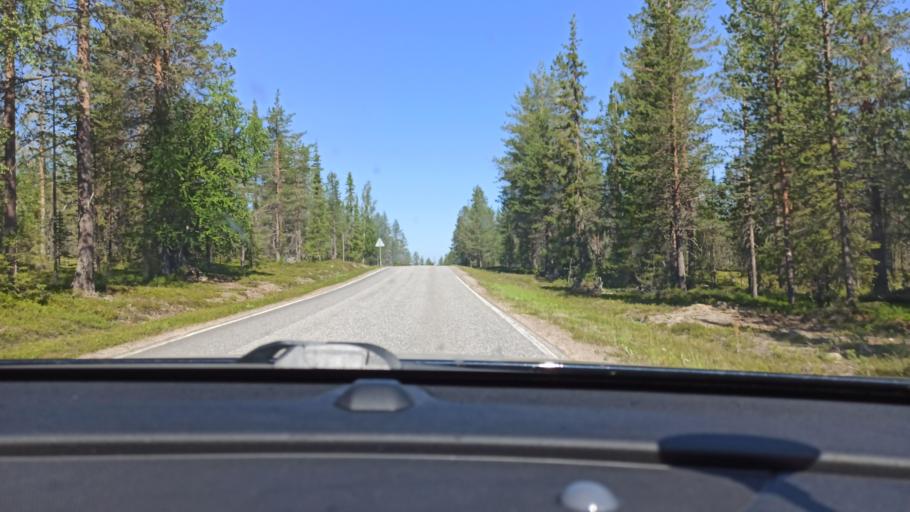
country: FI
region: Lapland
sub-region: Tunturi-Lappi
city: Kolari
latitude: 67.6798
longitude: 24.1393
